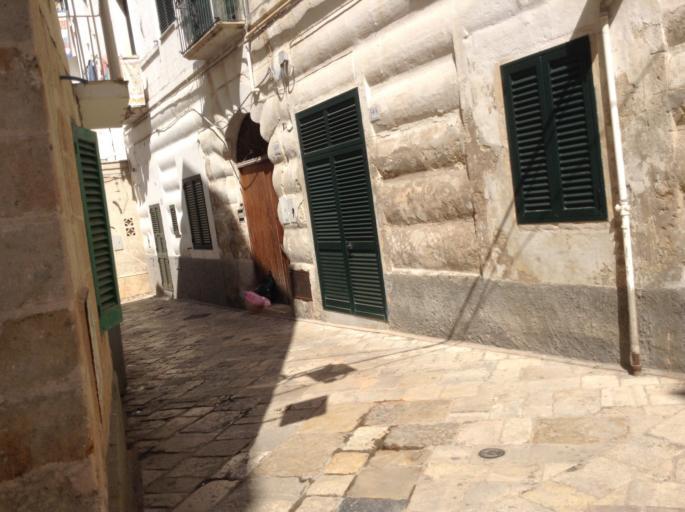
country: IT
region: Apulia
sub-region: Provincia di Bari
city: Monopoli
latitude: 40.9524
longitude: 17.3035
